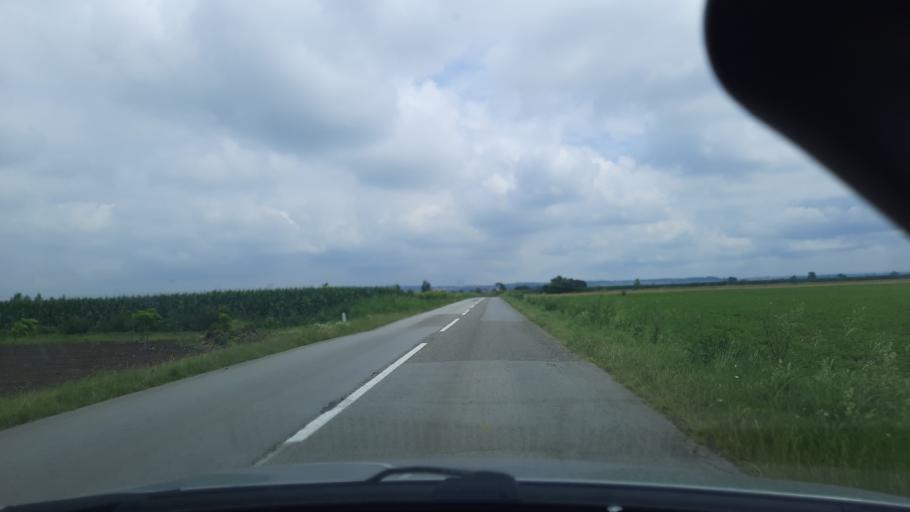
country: RS
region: Central Serbia
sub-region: Branicevski Okrug
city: Malo Crnice
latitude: 44.5812
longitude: 21.3148
